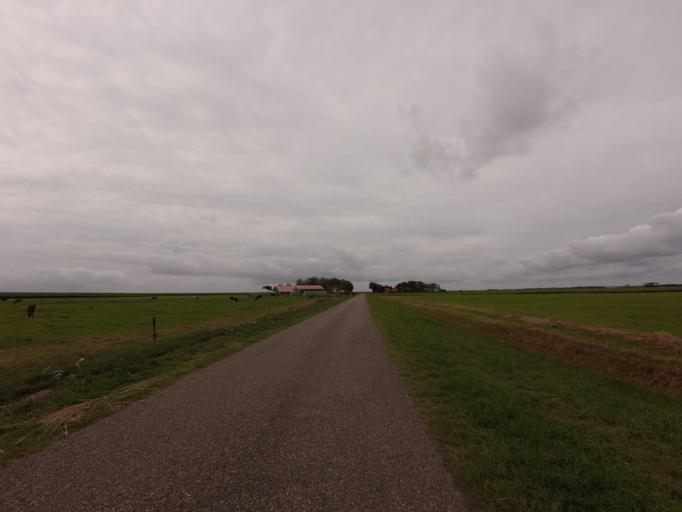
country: NL
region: Friesland
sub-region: Gemeente Ameland
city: Hollum
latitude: 53.4349
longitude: 5.7056
